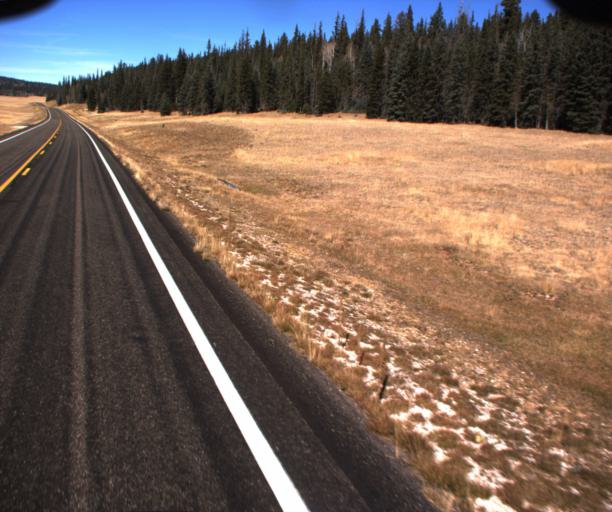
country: US
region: Arizona
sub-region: Coconino County
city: Grand Canyon
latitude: 36.3683
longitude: -112.1216
